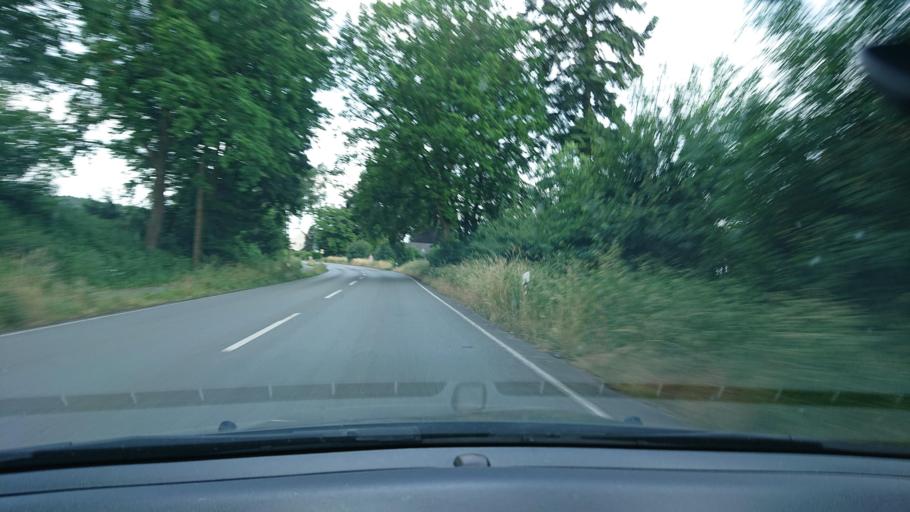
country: DE
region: North Rhine-Westphalia
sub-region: Regierungsbezirk Detmold
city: Hiddenhausen
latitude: 52.1623
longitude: 8.6362
